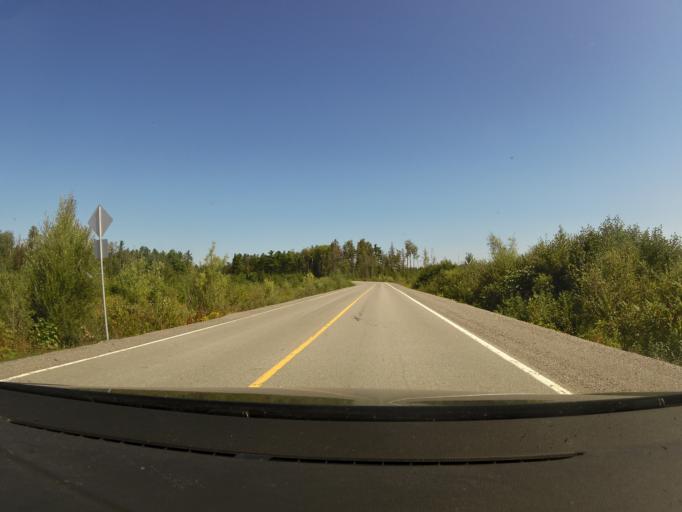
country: CA
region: Ontario
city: Bells Corners
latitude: 45.2528
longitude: -75.9746
